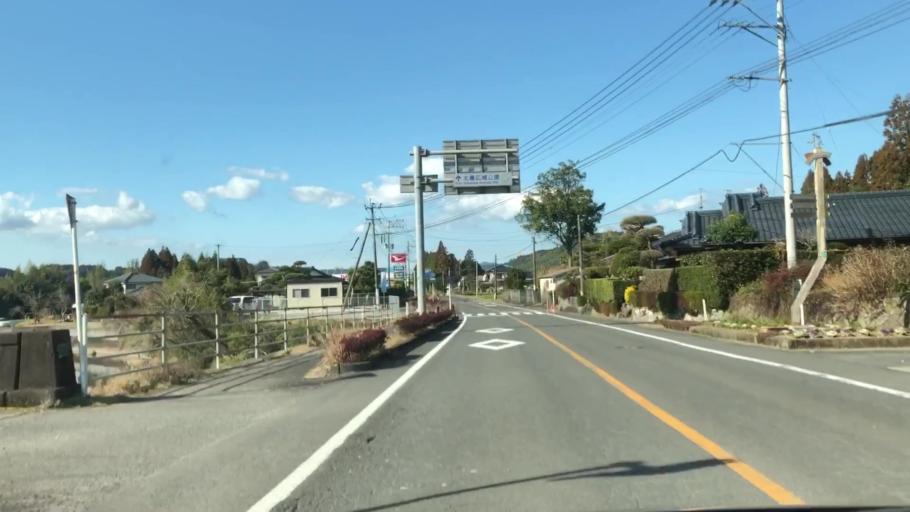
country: JP
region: Kagoshima
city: Satsumasendai
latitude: 31.7968
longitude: 130.4411
